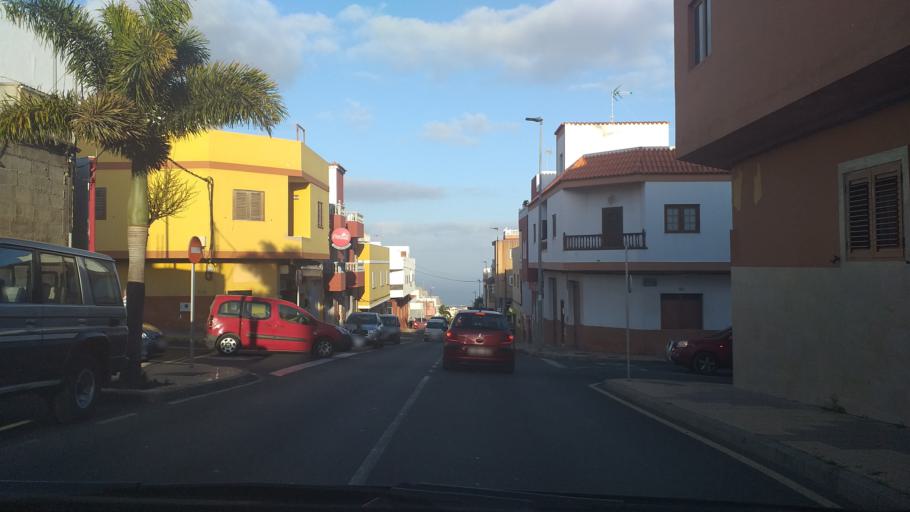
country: ES
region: Canary Islands
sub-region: Provincia de Las Palmas
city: Ingenio
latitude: 27.9180
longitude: -15.4446
